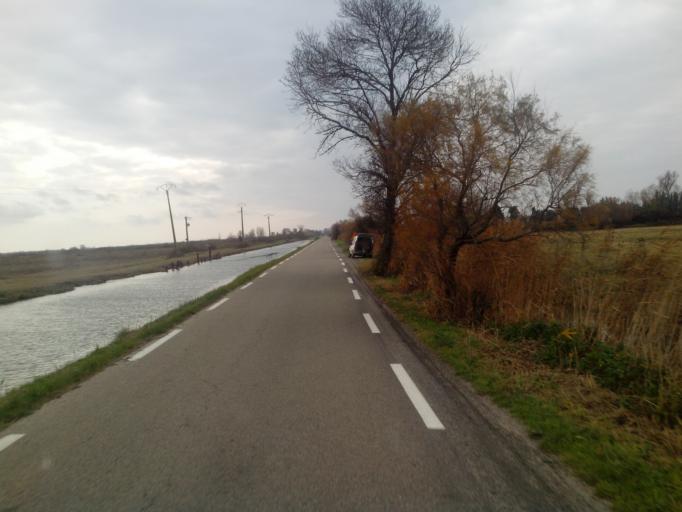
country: FR
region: Languedoc-Roussillon
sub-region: Departement du Gard
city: Vauvert
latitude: 43.6031
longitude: 4.3377
